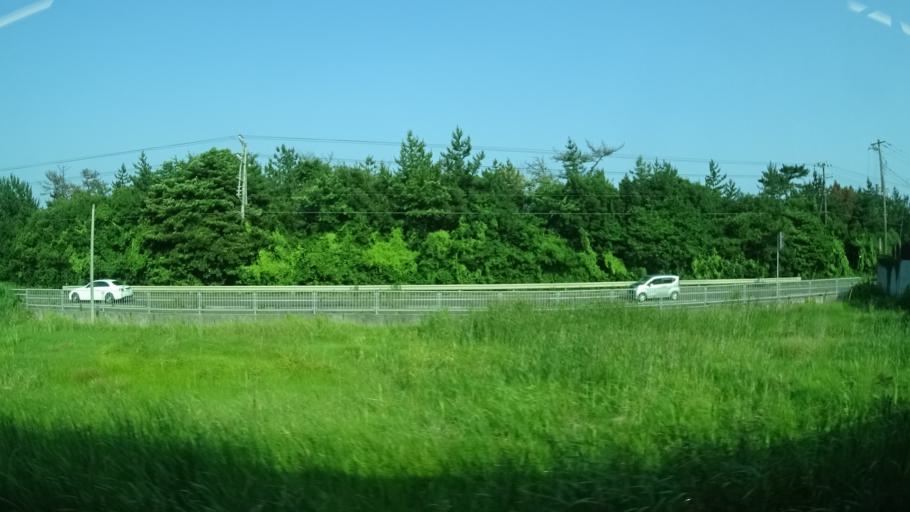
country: JP
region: Ibaraki
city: Kitaibaraki
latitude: 36.8132
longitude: 140.7641
